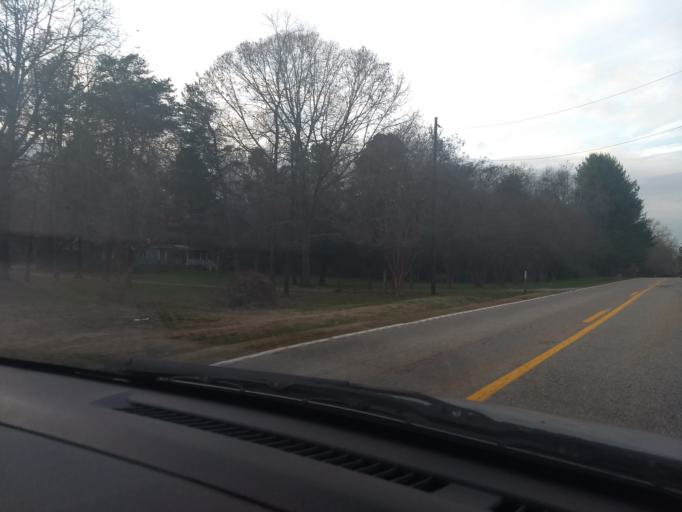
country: US
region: South Carolina
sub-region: Greenville County
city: Greer
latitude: 35.0052
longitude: -82.2152
